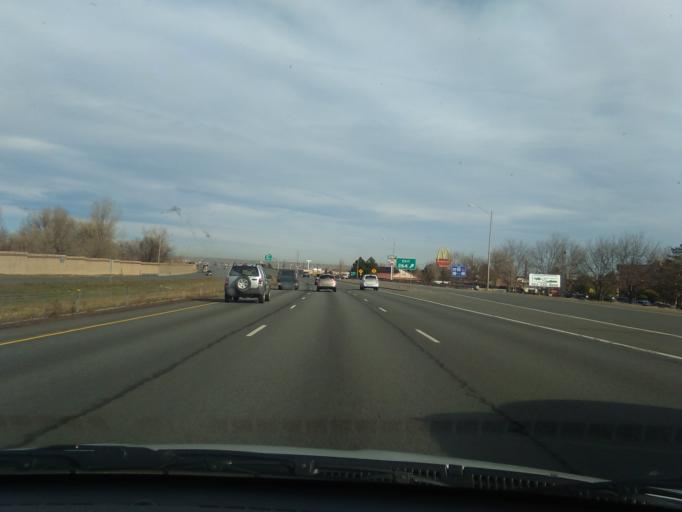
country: US
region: Colorado
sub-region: Jefferson County
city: Applewood
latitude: 39.7562
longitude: -105.1443
